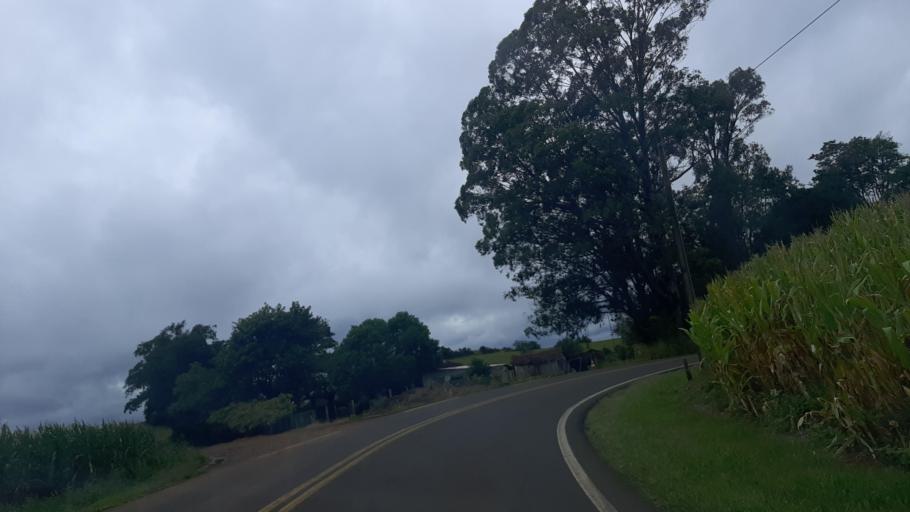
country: BR
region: Parana
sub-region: Ampere
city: Ampere
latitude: -25.9627
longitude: -53.4424
